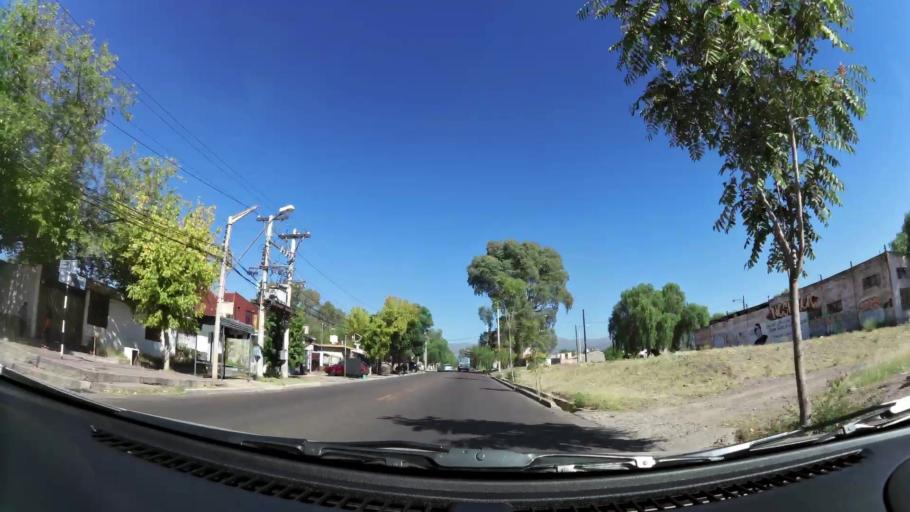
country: AR
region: Mendoza
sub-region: Departamento de Godoy Cruz
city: Godoy Cruz
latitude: -32.9014
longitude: -68.8813
